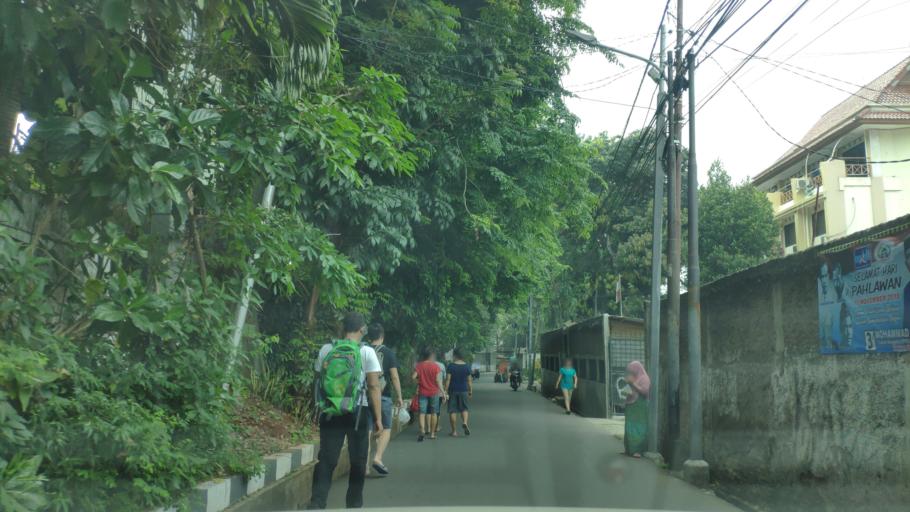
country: ID
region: Jakarta Raya
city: Jakarta
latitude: -6.1932
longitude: 106.8020
